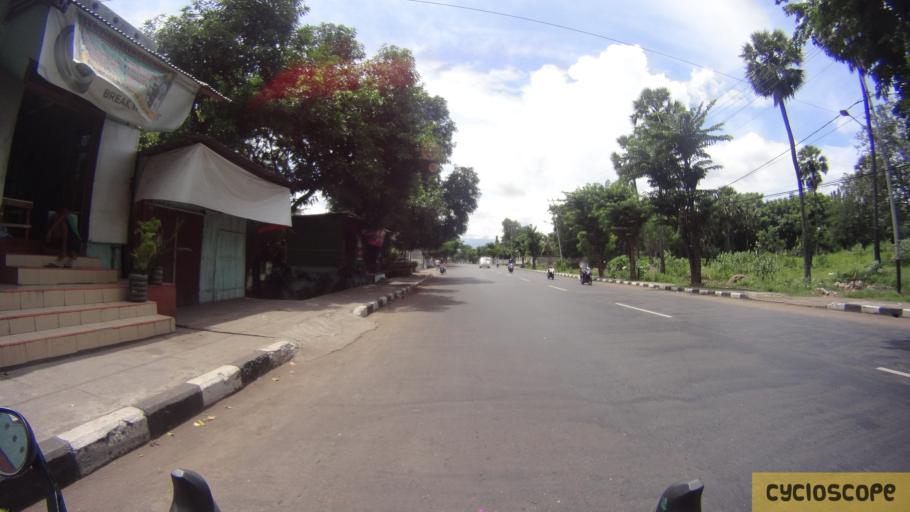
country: ID
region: East Nusa Tenggara
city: Waioti
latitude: -8.6267
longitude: 122.2314
